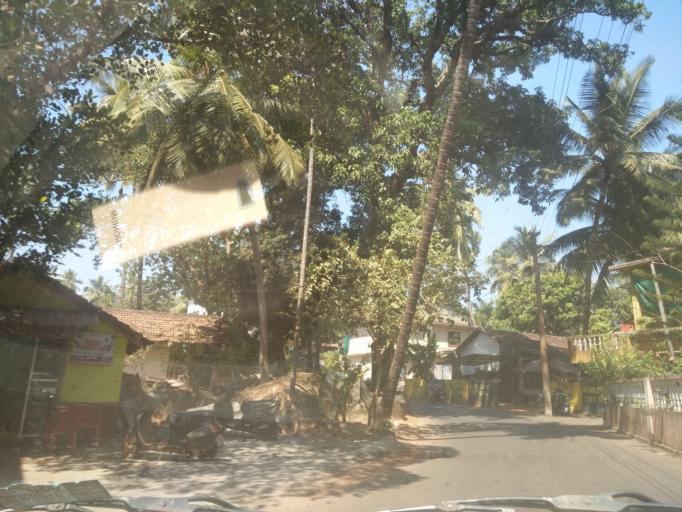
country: IN
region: Goa
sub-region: North Goa
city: Morjim
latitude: 15.6335
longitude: 73.7420
